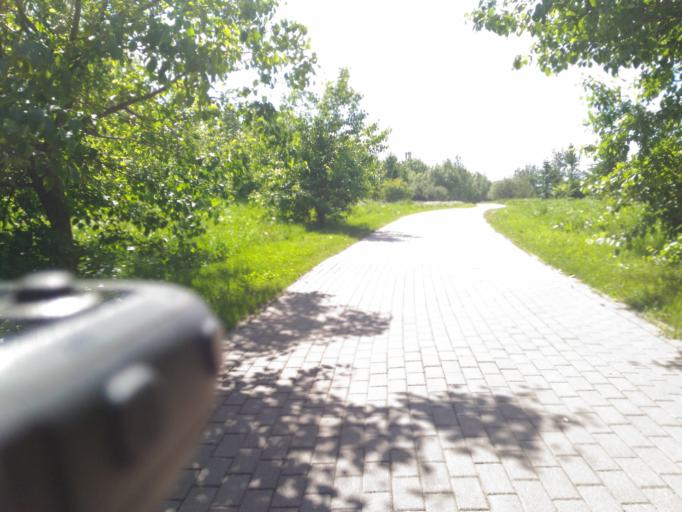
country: RU
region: Moscow
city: Shchukino
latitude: 55.7734
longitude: 37.4197
